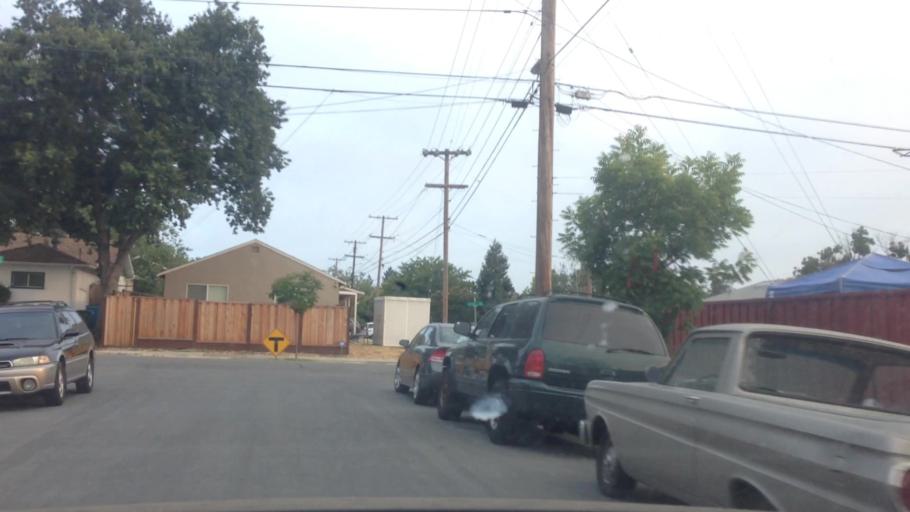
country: US
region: California
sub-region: San Mateo County
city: Redwood City
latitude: 37.4688
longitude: -122.2420
